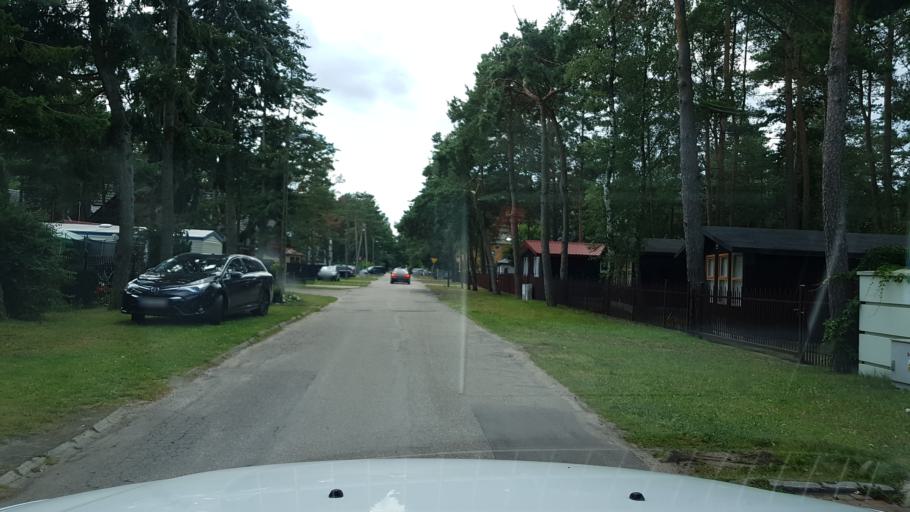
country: PL
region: West Pomeranian Voivodeship
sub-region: Powiat gryficki
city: Pobierowo
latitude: 54.0607
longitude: 14.9431
